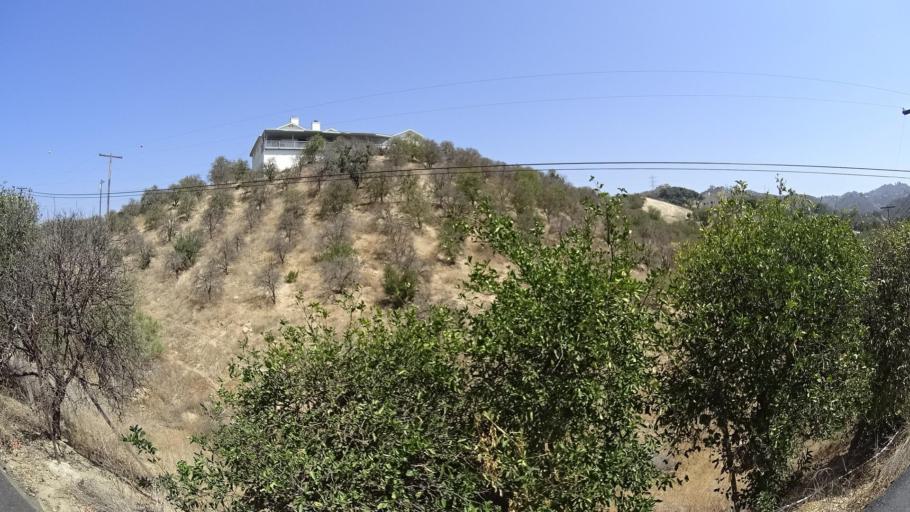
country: US
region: California
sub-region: San Diego County
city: Fallbrook
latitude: 33.4290
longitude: -117.3091
